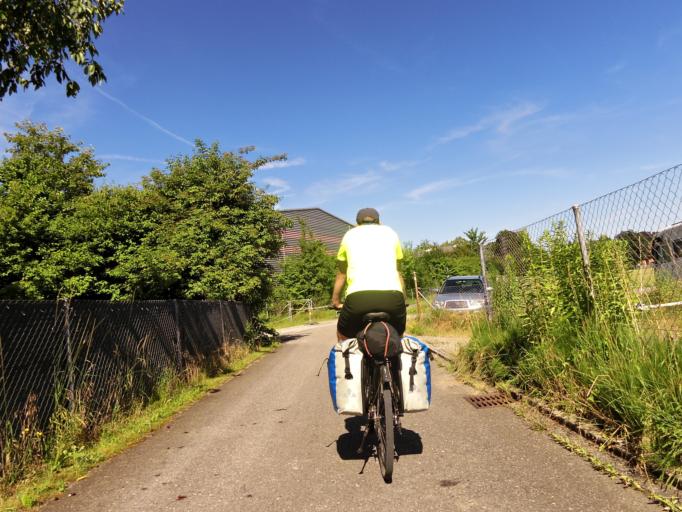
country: CH
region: Thurgau
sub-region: Kreuzlingen District
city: Kreuzlingen
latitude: 47.6463
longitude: 9.1913
